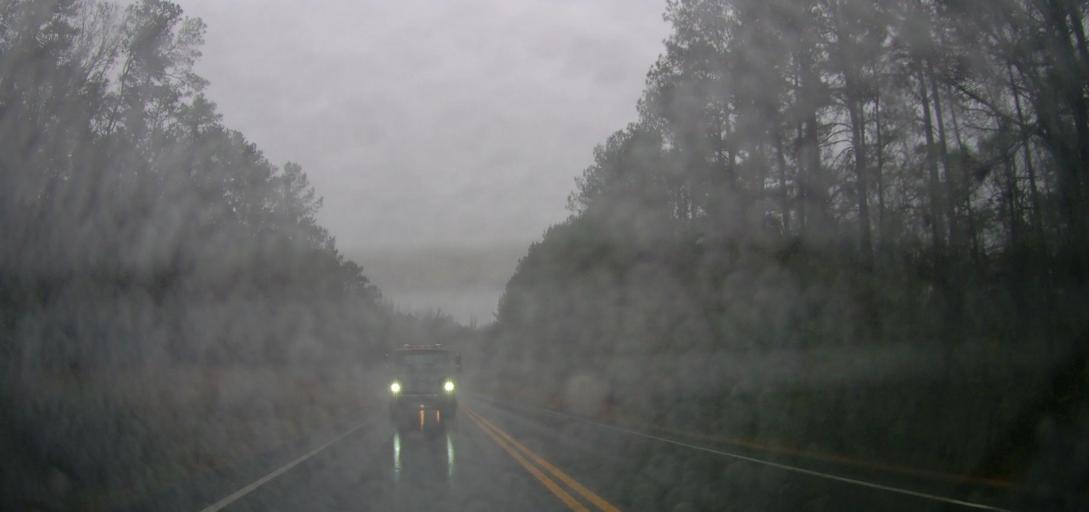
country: US
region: Georgia
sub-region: Putnam County
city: Eatonton
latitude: 33.1918
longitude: -83.4339
